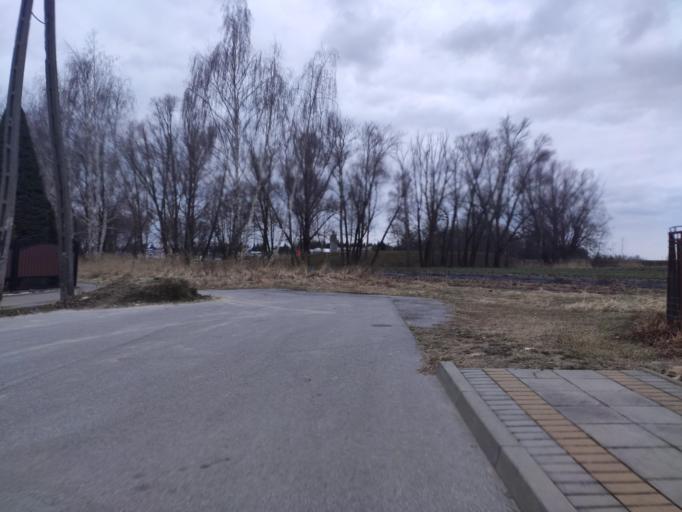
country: PL
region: Lublin Voivodeship
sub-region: Powiat lubartowski
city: Kock
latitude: 51.6431
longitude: 22.4405
